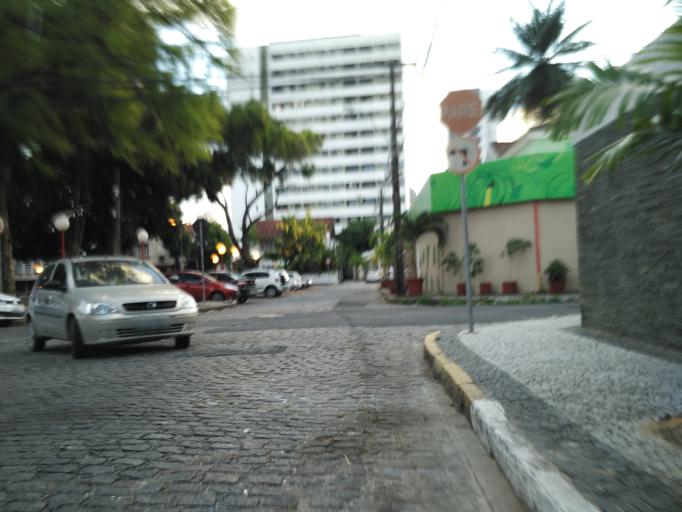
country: BR
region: Pernambuco
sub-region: Recife
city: Recife
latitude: -8.0335
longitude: -34.9116
